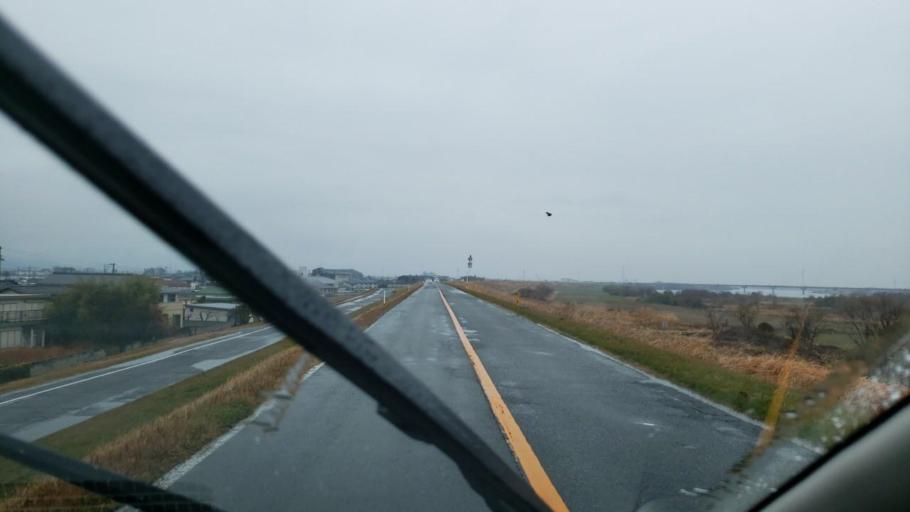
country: JP
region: Tokushima
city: Ishii
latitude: 34.1030
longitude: 134.4199
